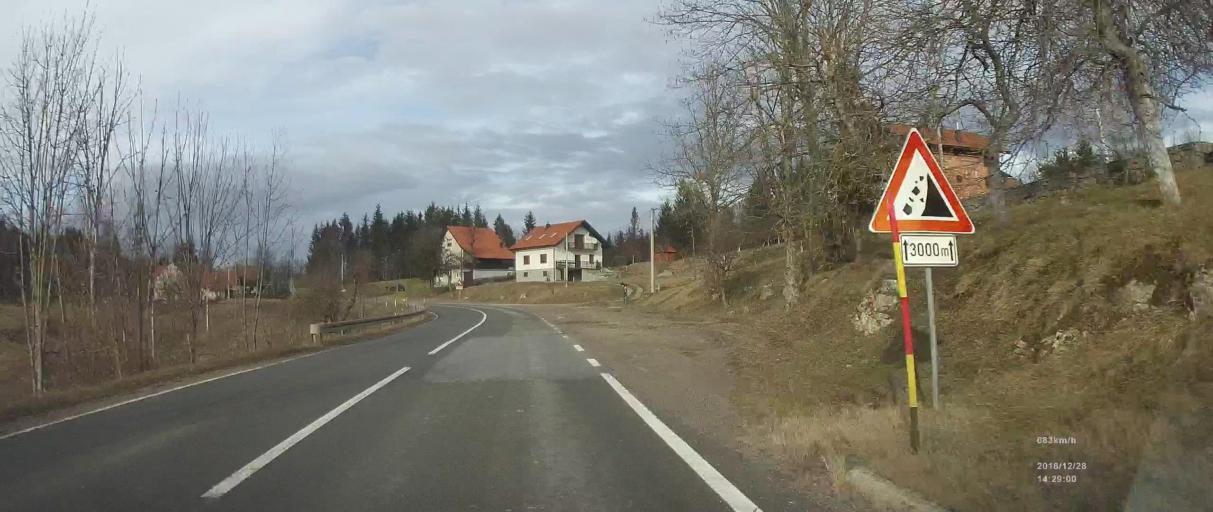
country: HR
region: Primorsko-Goranska
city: Vrbovsko
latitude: 45.4165
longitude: 15.1169
